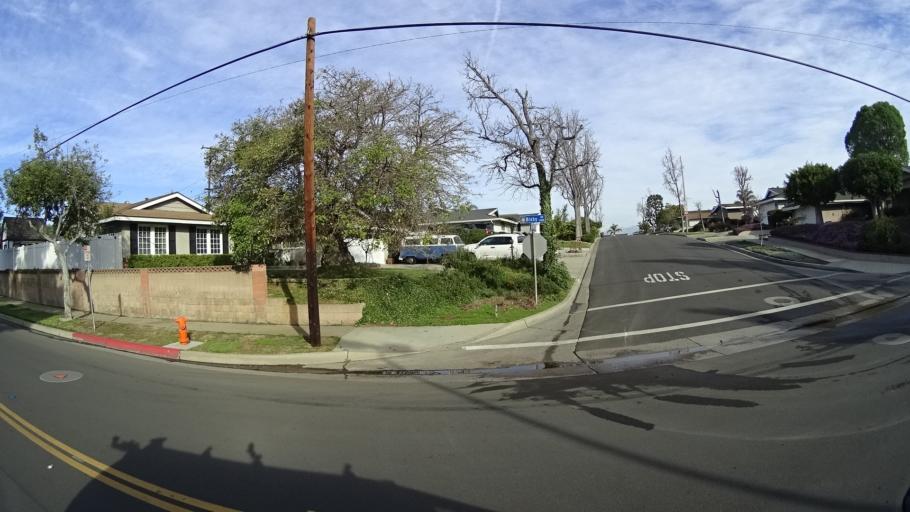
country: US
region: California
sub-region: Orange County
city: Villa Park
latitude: 33.8389
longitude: -117.8383
